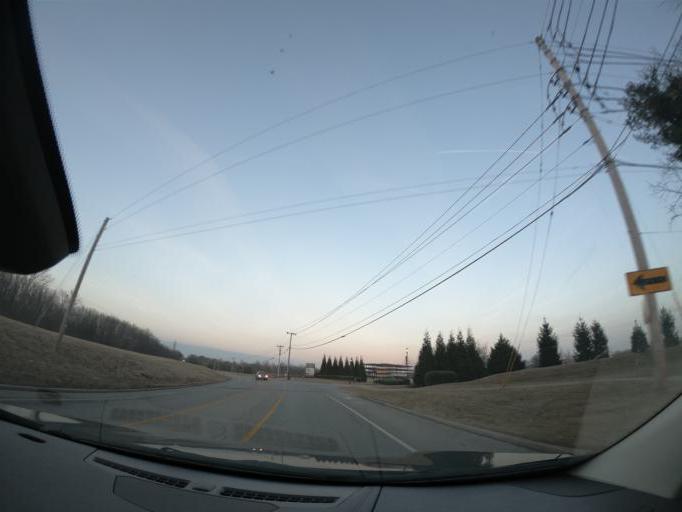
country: US
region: Kentucky
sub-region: Jefferson County
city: Lyndon
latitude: 38.2563
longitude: -85.5874
